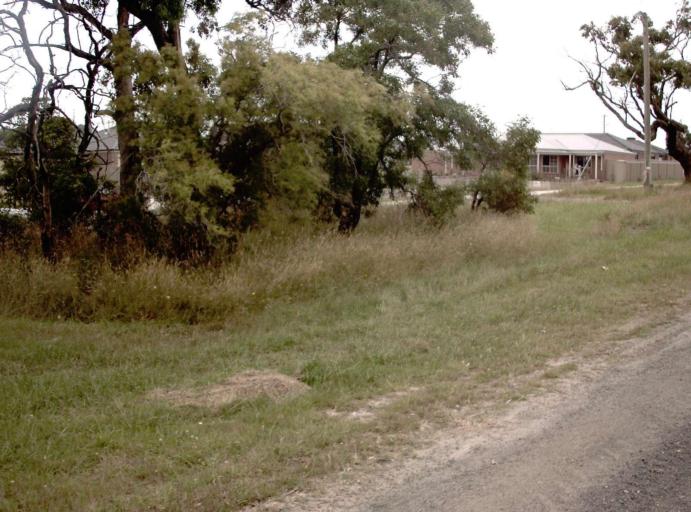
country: AU
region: Victoria
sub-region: Cardinia
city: Officer
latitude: -38.0604
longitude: 145.4472
